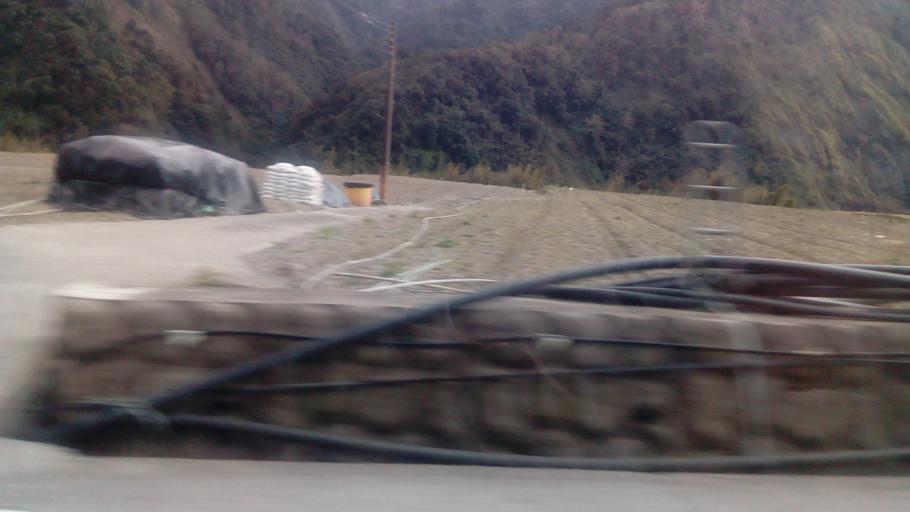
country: TW
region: Taiwan
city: Daxi
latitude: 24.4691
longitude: 121.4072
